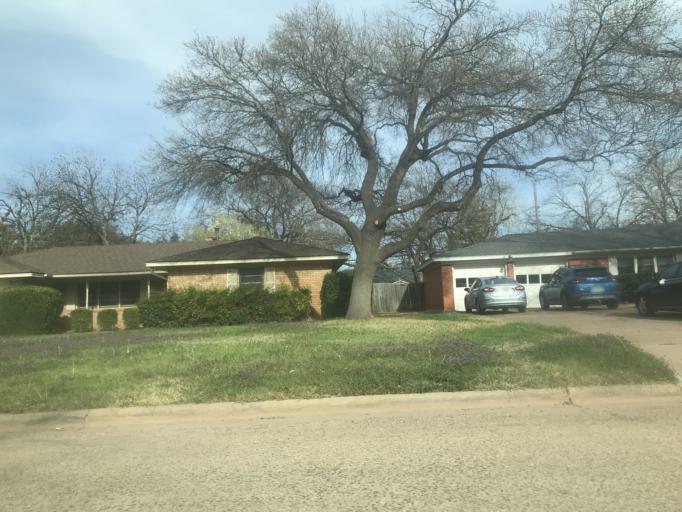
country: US
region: Texas
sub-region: Taylor County
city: Abilene
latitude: 32.4227
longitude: -99.7720
